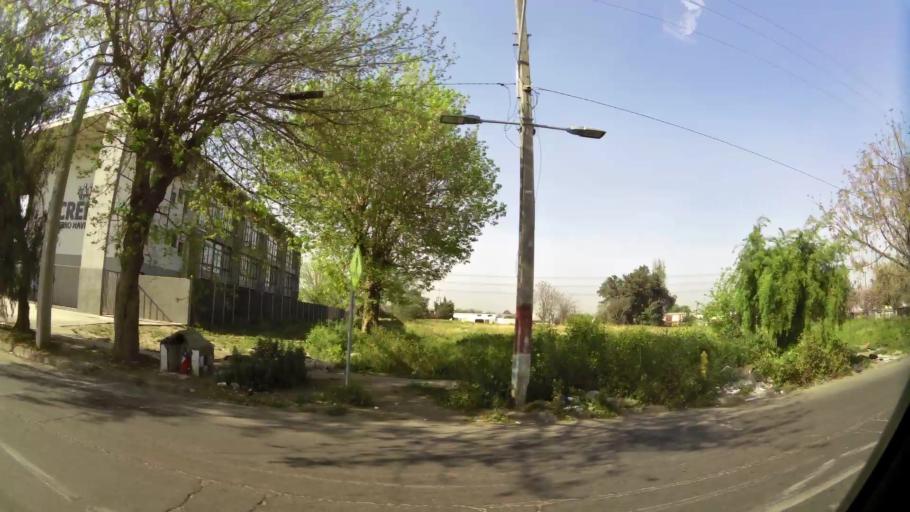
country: CL
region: Santiago Metropolitan
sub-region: Provincia de Santiago
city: Lo Prado
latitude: -33.4230
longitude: -70.7571
